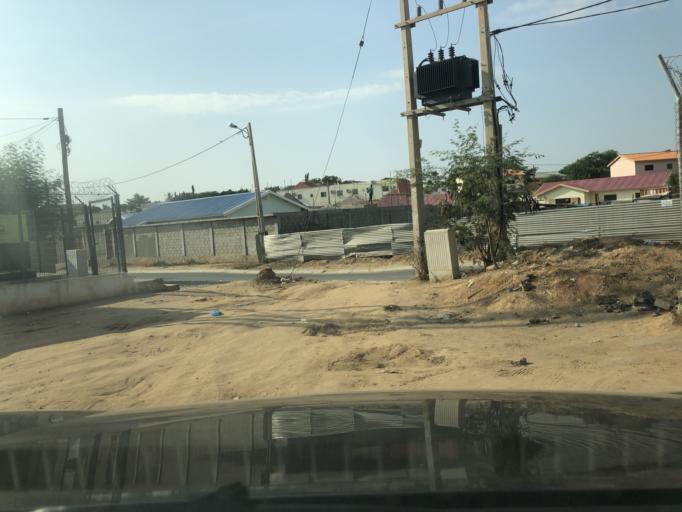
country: AO
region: Luanda
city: Luanda
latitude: -8.9110
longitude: 13.2263
